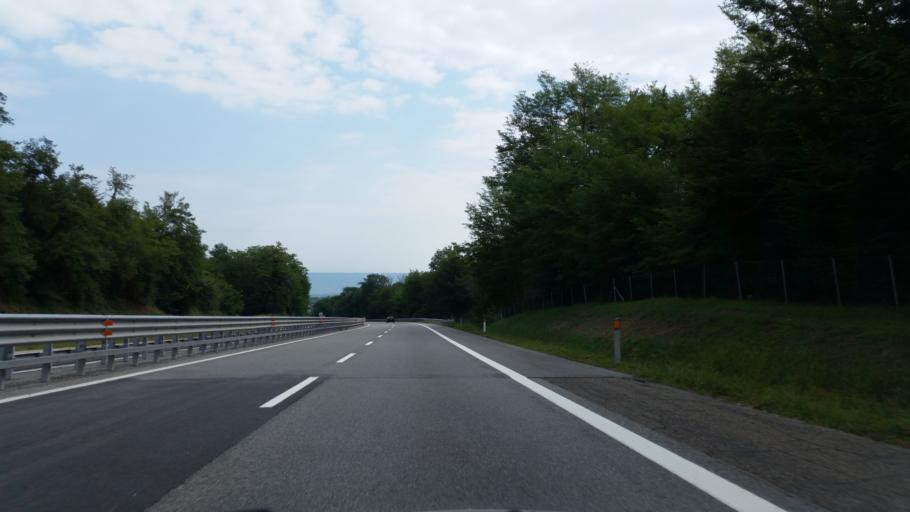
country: IT
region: Piedmont
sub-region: Provincia di Torino
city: Scarmagno
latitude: 45.3706
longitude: 7.8415
